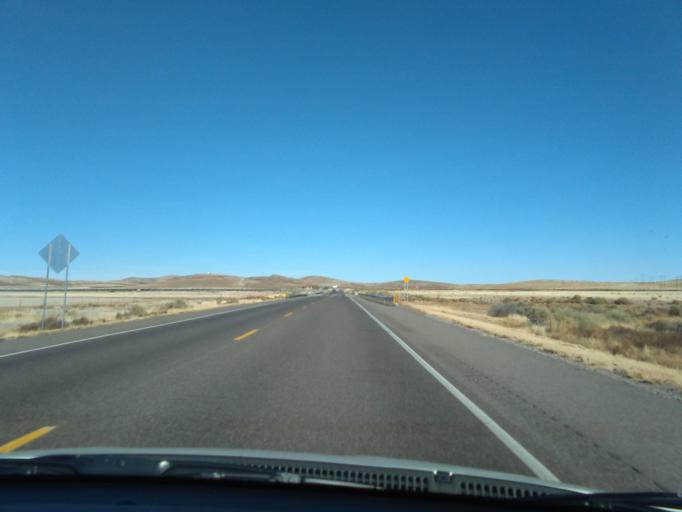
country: US
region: New Mexico
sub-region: Dona Ana County
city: Hatch
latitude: 32.5653
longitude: -107.4641
